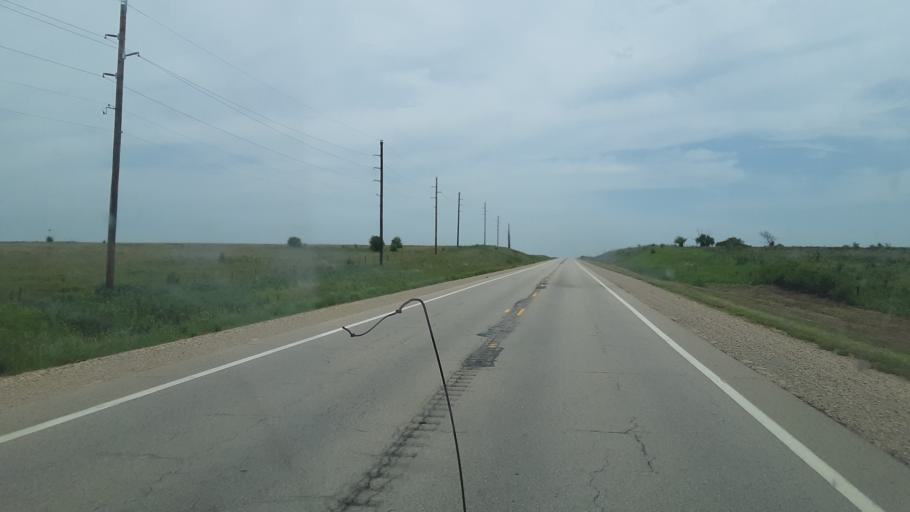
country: US
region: Kansas
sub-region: Greenwood County
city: Eureka
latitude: 37.8387
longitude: -96.1605
